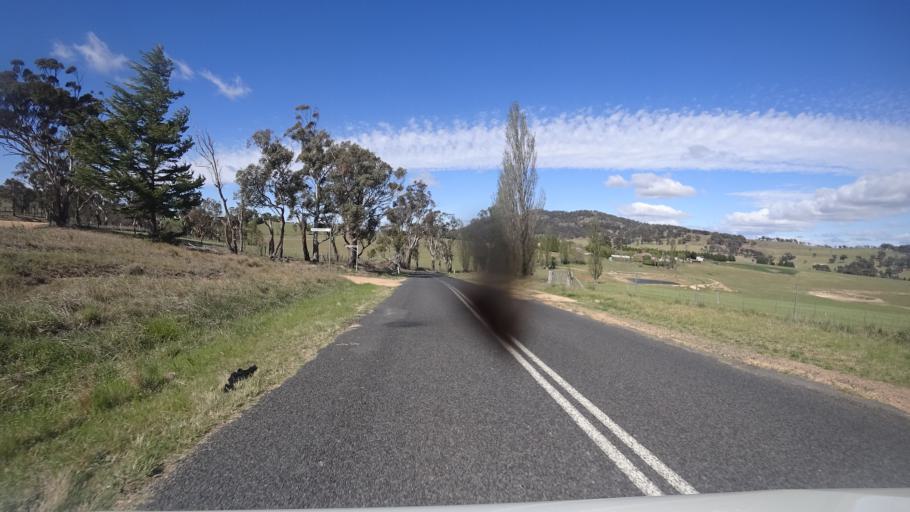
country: AU
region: New South Wales
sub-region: Lithgow
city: Portland
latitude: -33.5212
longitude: 149.9456
